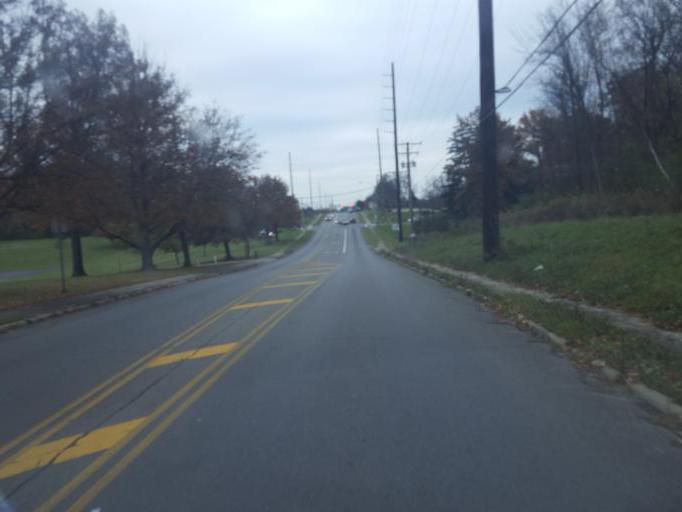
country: US
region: Ohio
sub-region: Richland County
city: Mansfield
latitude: 40.7491
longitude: -82.5518
